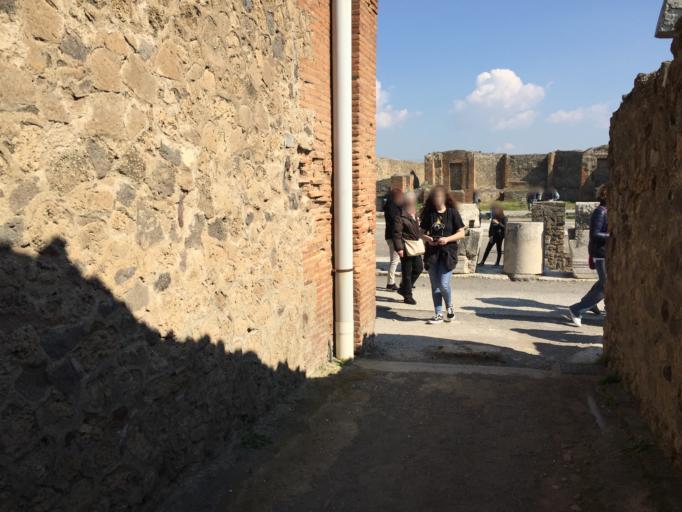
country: IT
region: Campania
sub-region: Provincia di Napoli
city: Pompei
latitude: 40.7490
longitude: 14.4836
